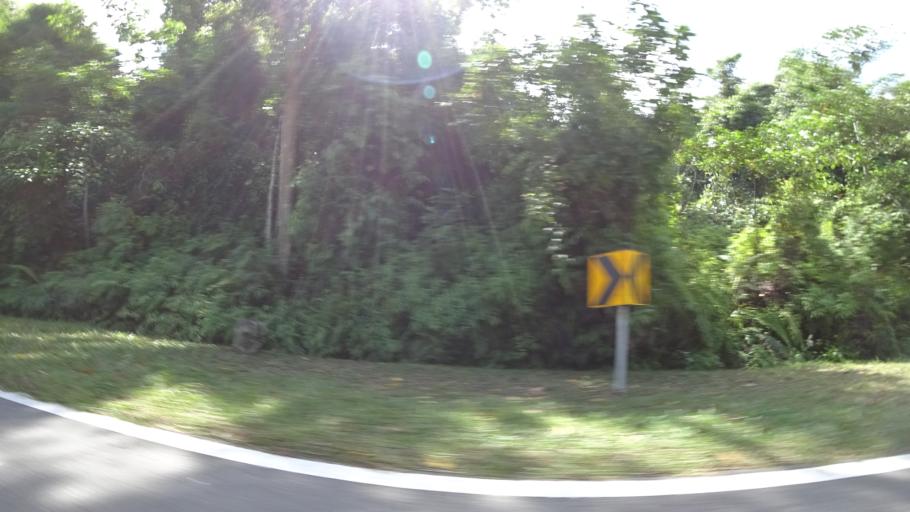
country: BN
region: Brunei and Muara
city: Bandar Seri Begawan
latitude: 4.8847
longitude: 114.9664
